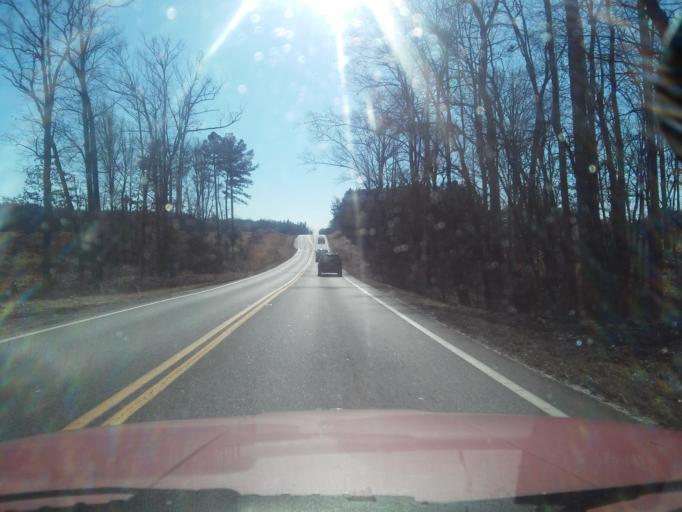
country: US
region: Virginia
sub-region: Orange County
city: Gordonsville
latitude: 37.9966
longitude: -78.1966
